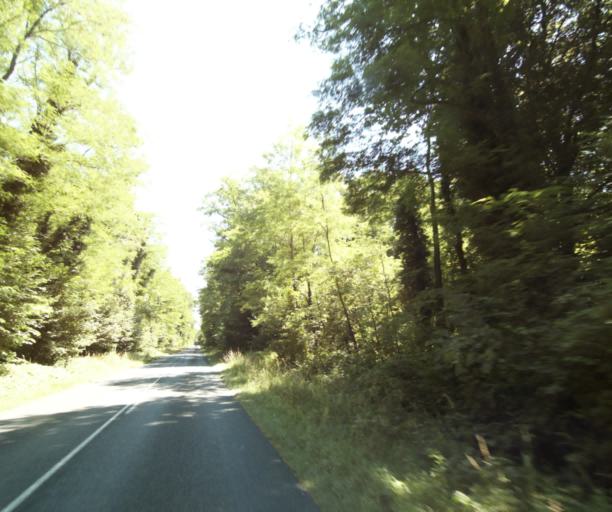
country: FR
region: Ile-de-France
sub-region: Departement de Seine-et-Marne
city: Noisy-sur-Ecole
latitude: 48.3769
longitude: 2.5021
